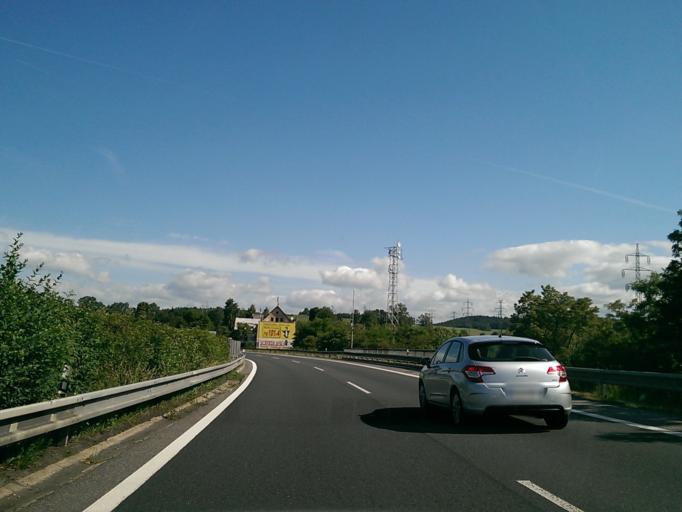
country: CZ
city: Ohrazenice
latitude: 50.6330
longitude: 15.1110
